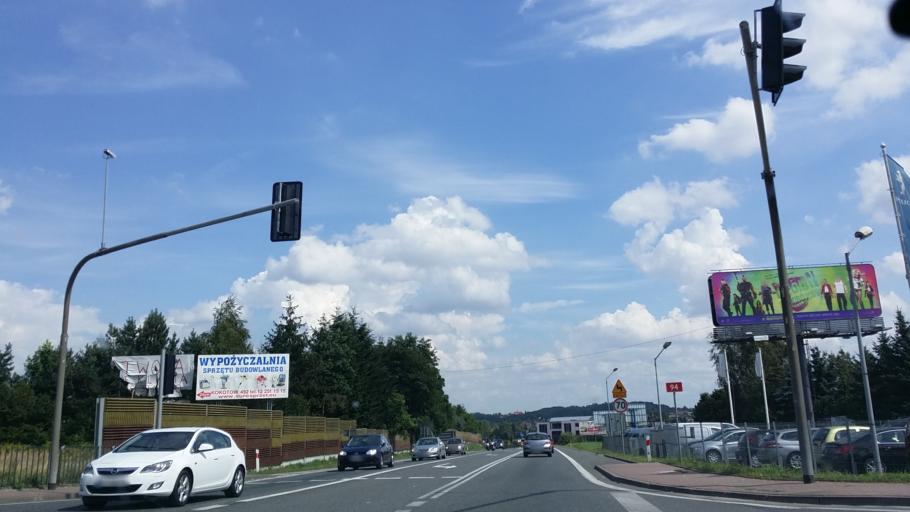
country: PL
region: Lesser Poland Voivodeship
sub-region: Powiat wielicki
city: Wieliczka
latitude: 49.9949
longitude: 20.0665
